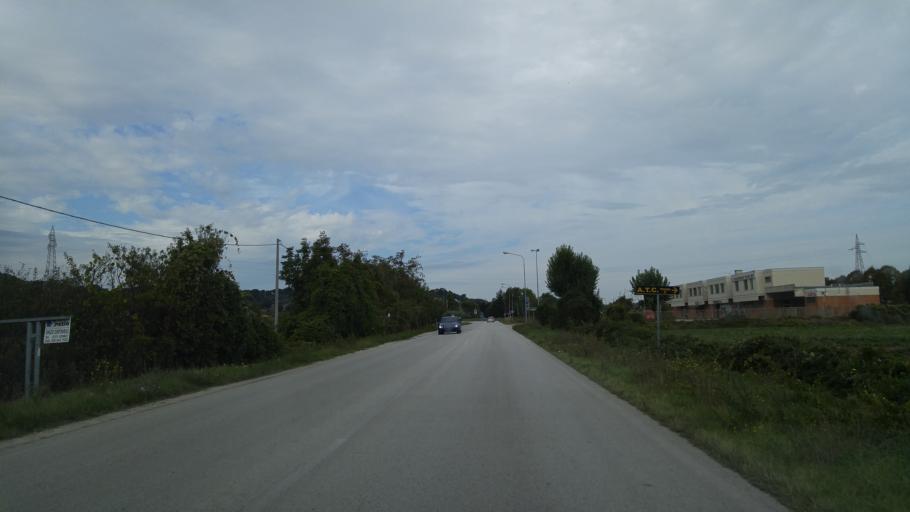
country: IT
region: The Marches
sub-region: Provincia di Pesaro e Urbino
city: Rosciano
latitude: 43.8140
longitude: 13.0012
